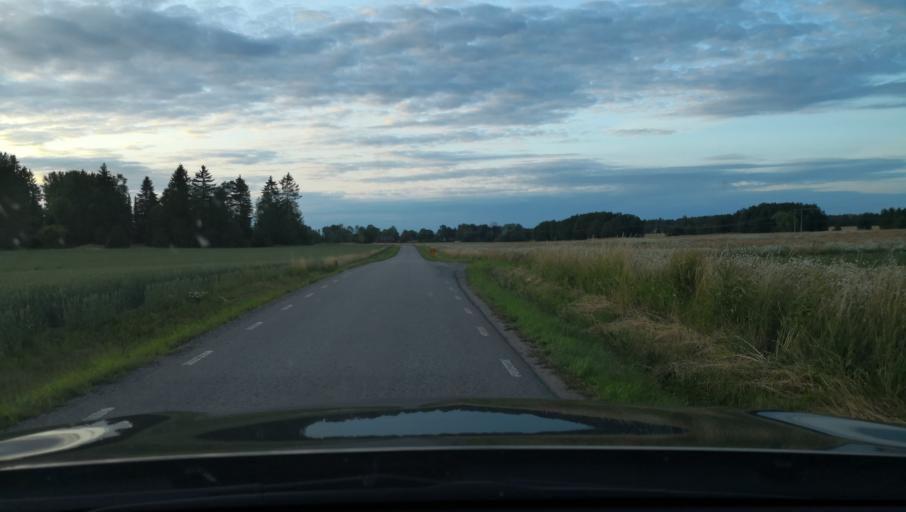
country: SE
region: Uppsala
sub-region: Uppsala Kommun
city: Vattholma
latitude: 60.0297
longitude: 17.6645
